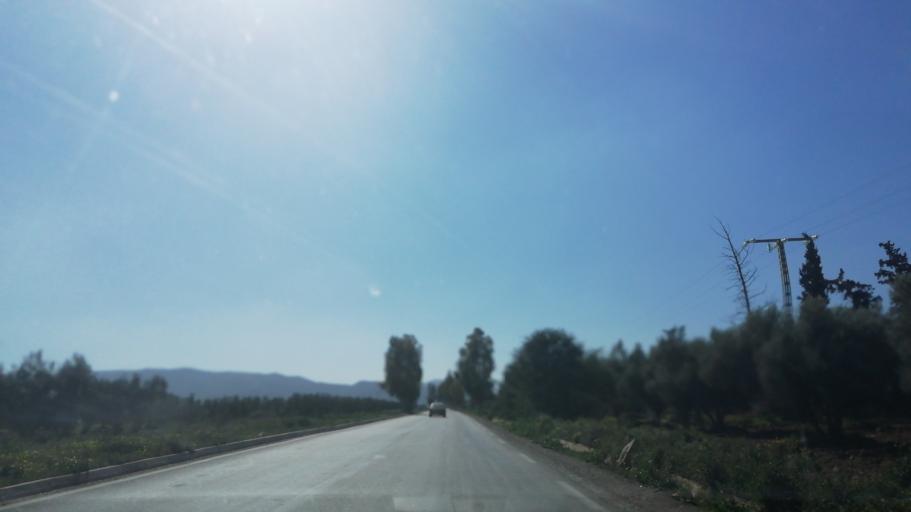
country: DZ
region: Mascara
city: Sig
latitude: 35.5545
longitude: -0.2069
